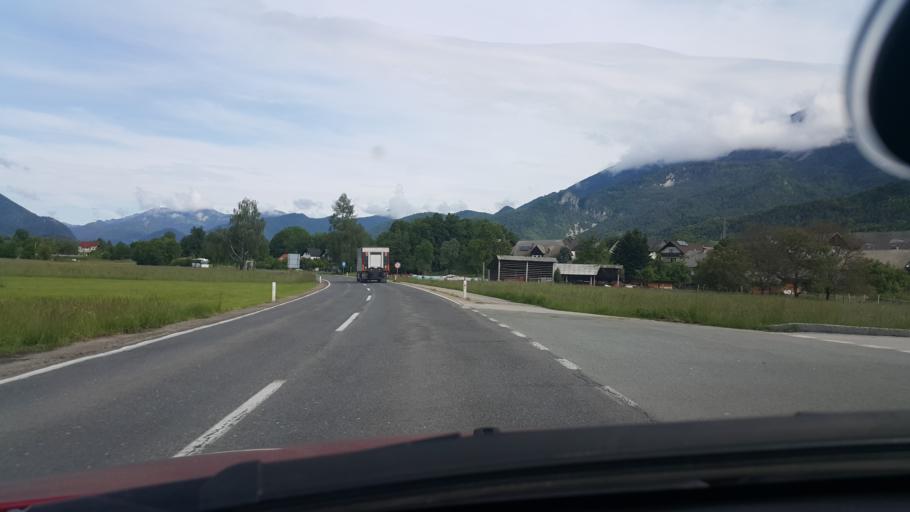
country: SI
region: Zirovnica
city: Zirovnica
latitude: 46.3864
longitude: 14.1467
